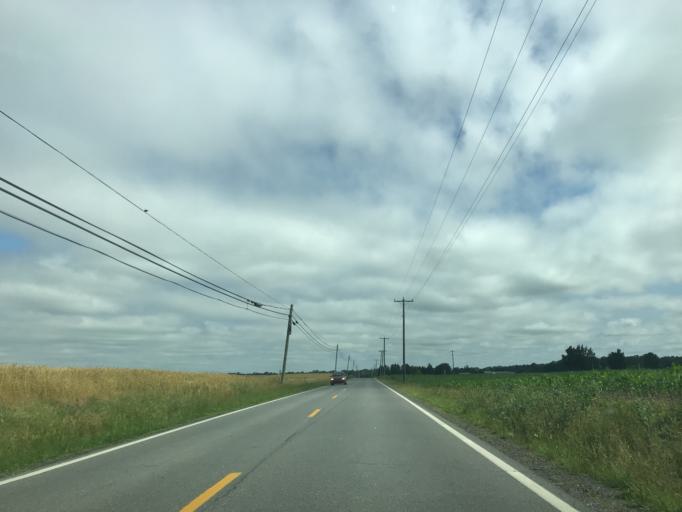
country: US
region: Maryland
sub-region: Caroline County
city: Ridgely
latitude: 38.8964
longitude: -75.9595
